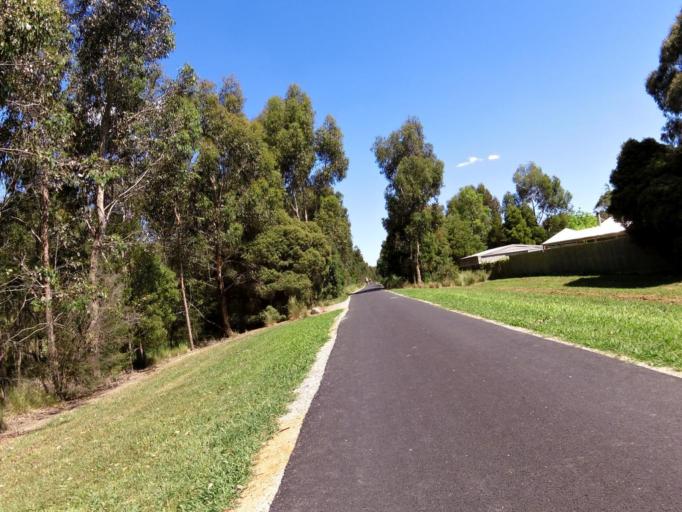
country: AU
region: Victoria
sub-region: Knox
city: Knoxfield
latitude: -37.8941
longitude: 145.2700
